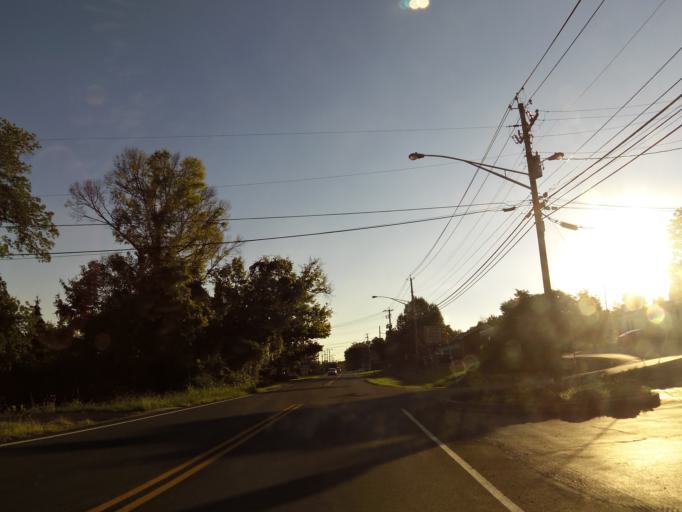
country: US
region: Tennessee
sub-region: Knox County
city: Knoxville
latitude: 35.9308
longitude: -84.0081
